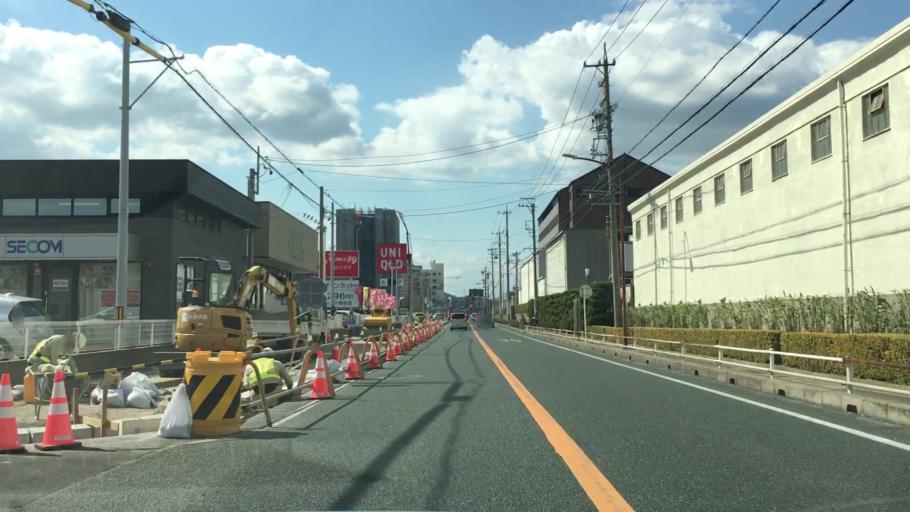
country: JP
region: Aichi
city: Gamagori
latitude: 34.8210
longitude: 137.2292
